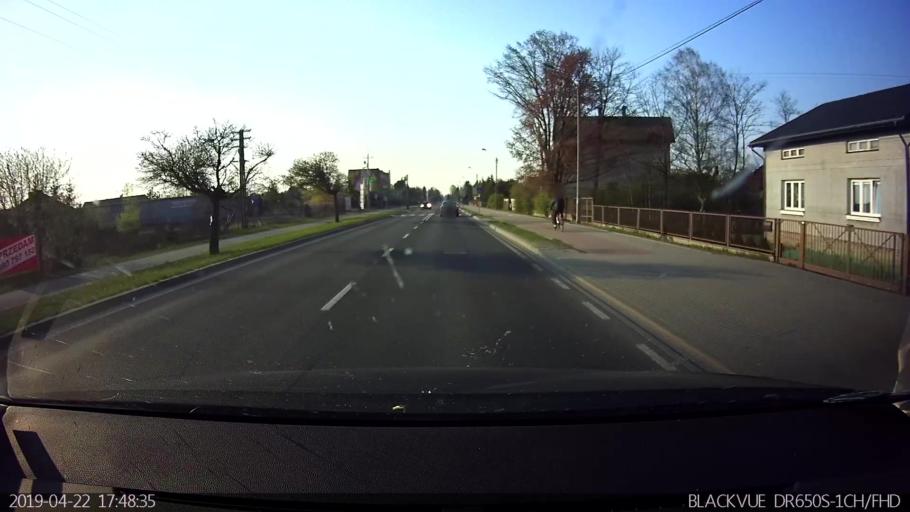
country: PL
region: Masovian Voivodeship
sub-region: Powiat wegrowski
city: Wegrow
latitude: 52.4063
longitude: 22.0137
